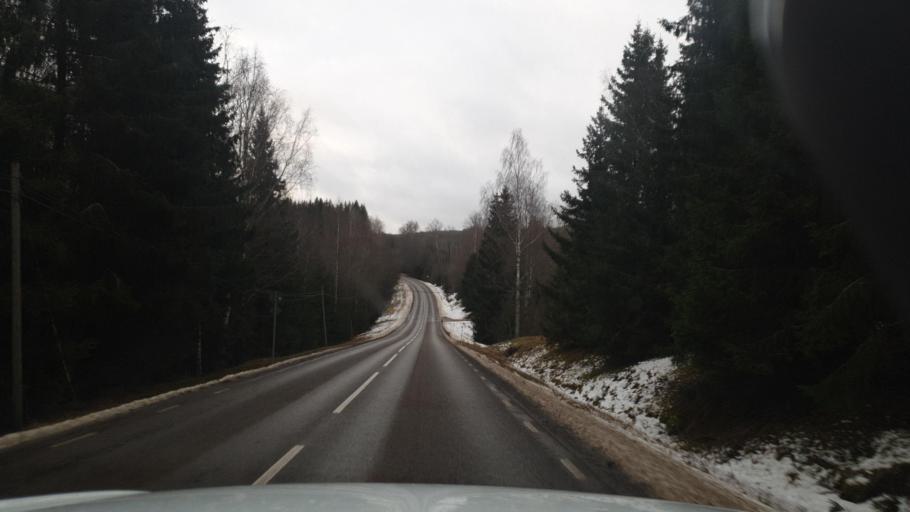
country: SE
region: Vaermland
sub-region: Eda Kommun
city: Amotfors
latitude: 59.7402
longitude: 12.3810
